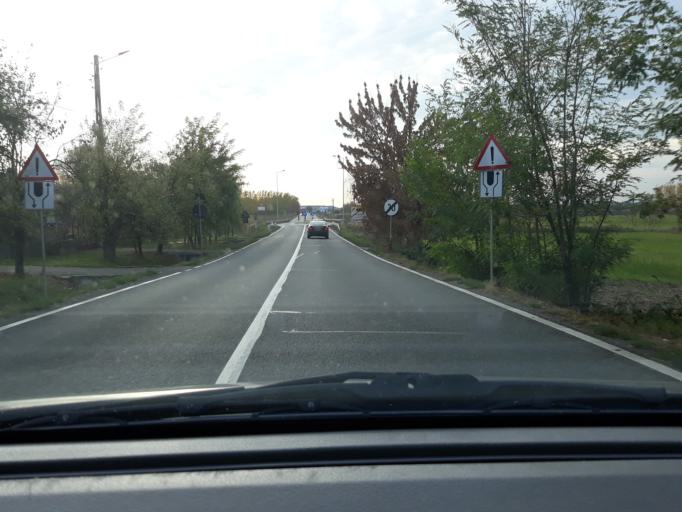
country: RO
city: Szekelyhid
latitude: 47.3313
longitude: 22.0846
